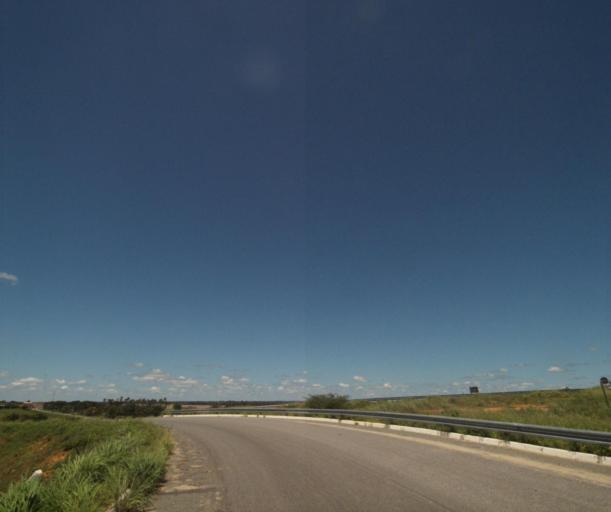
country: BR
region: Bahia
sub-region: Carinhanha
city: Carinhanha
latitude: -14.3276
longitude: -43.7648
